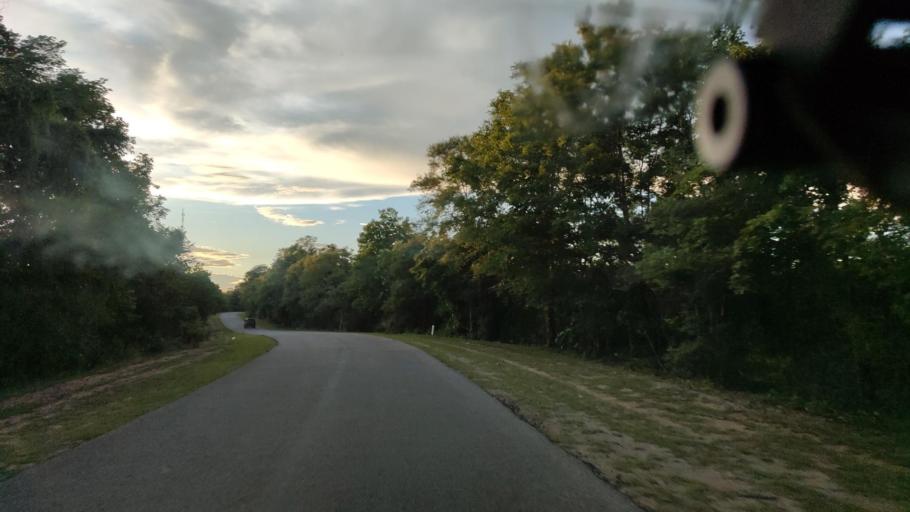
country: MM
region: Magway
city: Taungdwingyi
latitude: 20.1523
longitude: 95.6221
